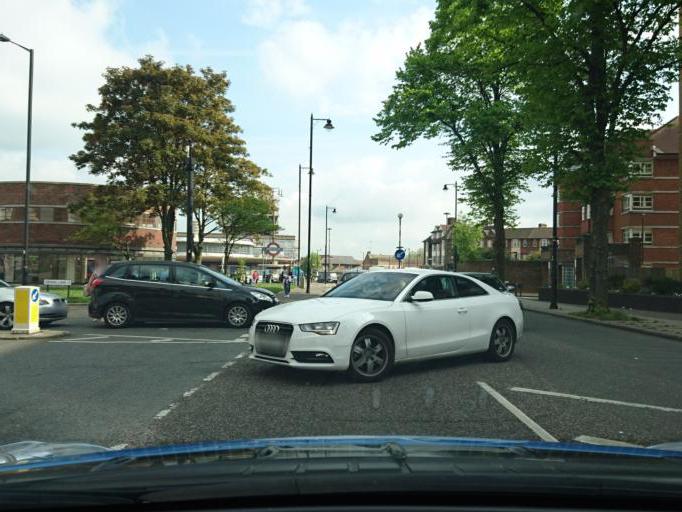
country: GB
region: England
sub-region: Greater London
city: Wood Green
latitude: 51.6314
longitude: -0.1278
